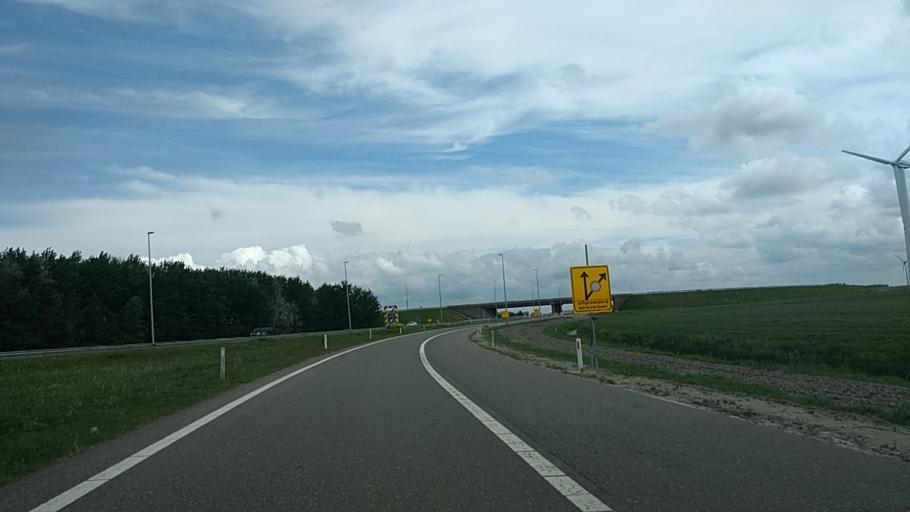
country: NL
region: Friesland
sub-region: Sudwest Fryslan
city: Makkum
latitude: 53.0961
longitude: 5.3878
